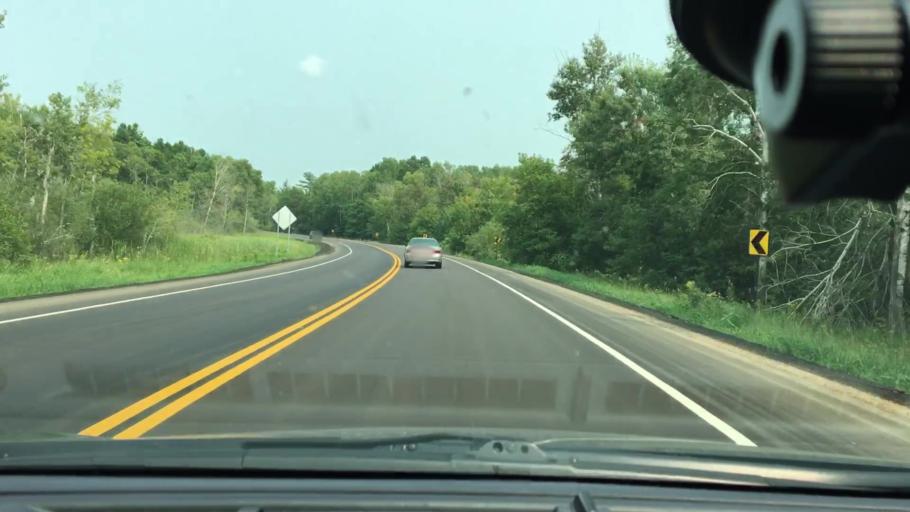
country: US
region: Minnesota
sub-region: Crow Wing County
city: Nisswa
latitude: 46.5220
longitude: -94.2753
